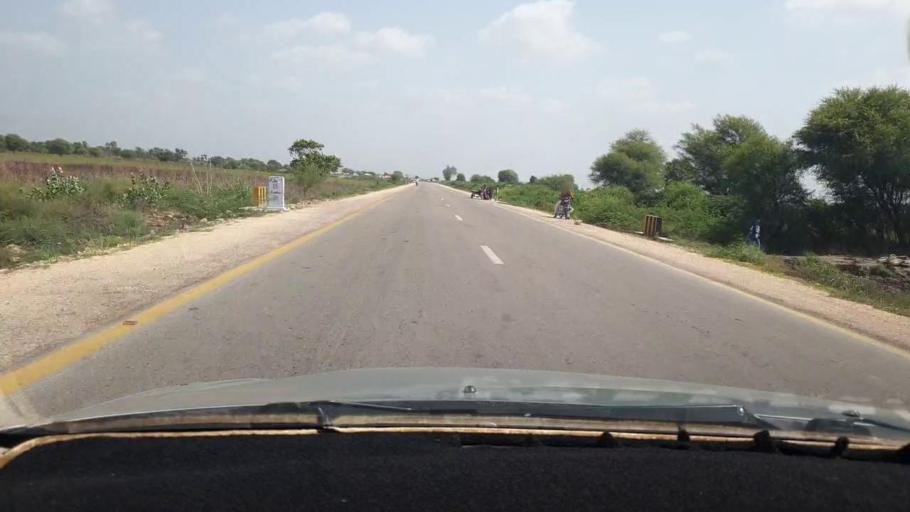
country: PK
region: Sindh
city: Digri
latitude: 25.1039
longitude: 69.1689
